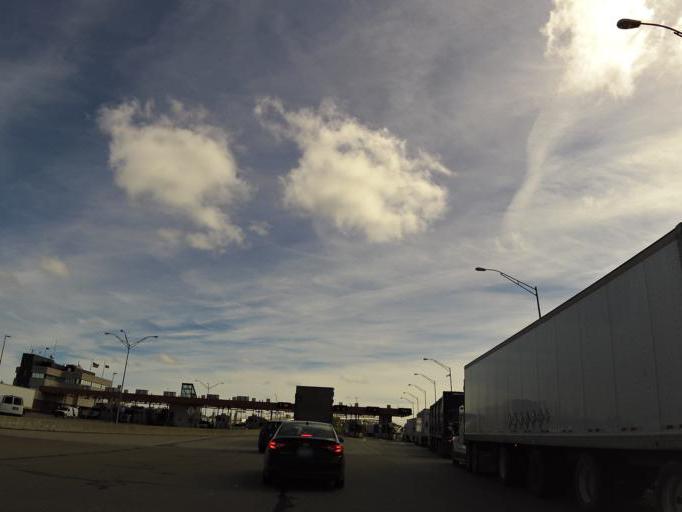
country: US
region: Michigan
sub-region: Saint Clair County
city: Port Huron
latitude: 42.9980
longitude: -82.4370
